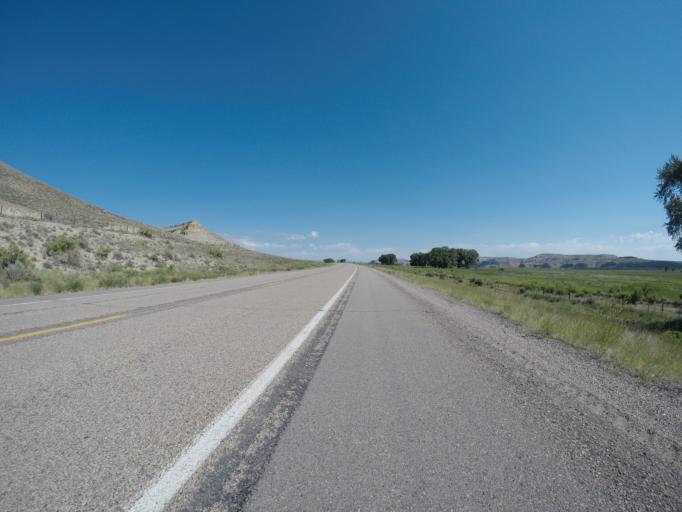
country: US
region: Wyoming
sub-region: Sublette County
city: Marbleton
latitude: 42.1963
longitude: -110.1783
